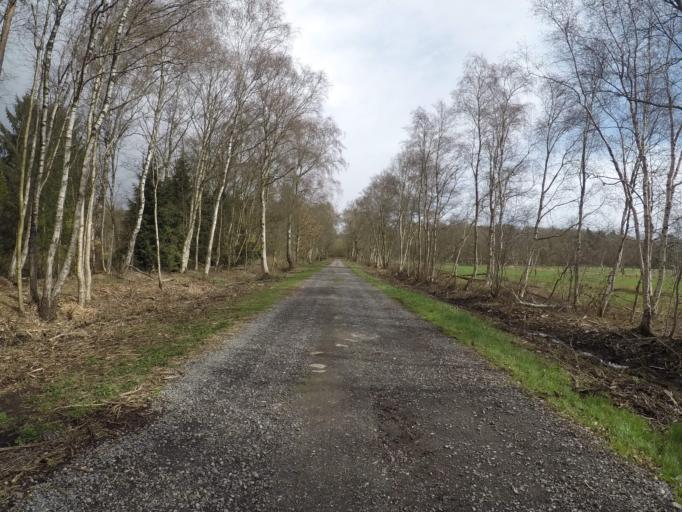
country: DE
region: Lower Saxony
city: Elmlohe
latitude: 53.6039
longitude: 8.7206
